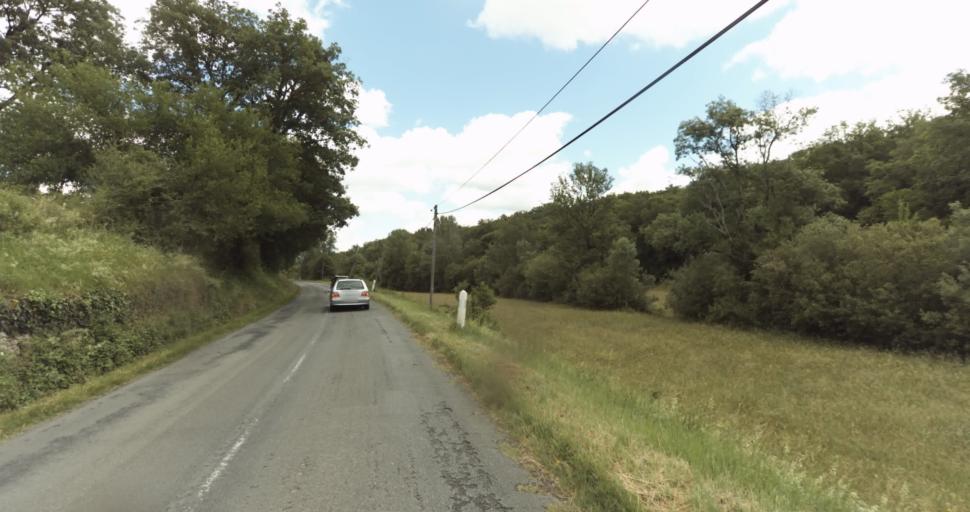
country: FR
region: Aquitaine
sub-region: Departement de la Dordogne
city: Beaumont-du-Perigord
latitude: 44.7507
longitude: 0.7608
